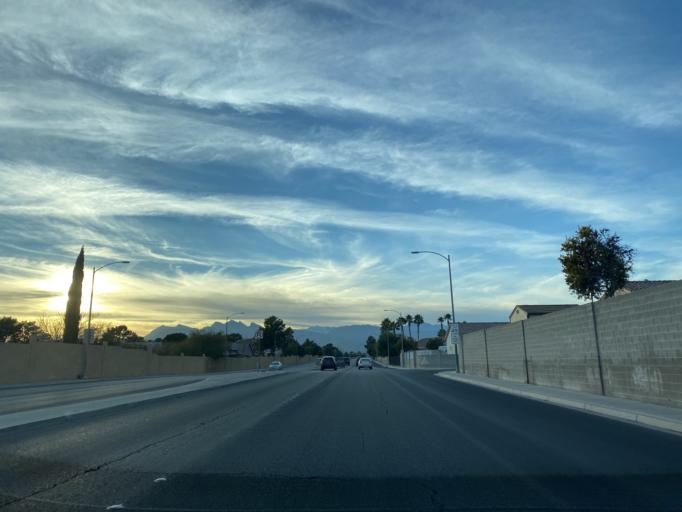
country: US
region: Nevada
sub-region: Clark County
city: North Las Vegas
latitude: 36.2611
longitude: -115.2171
